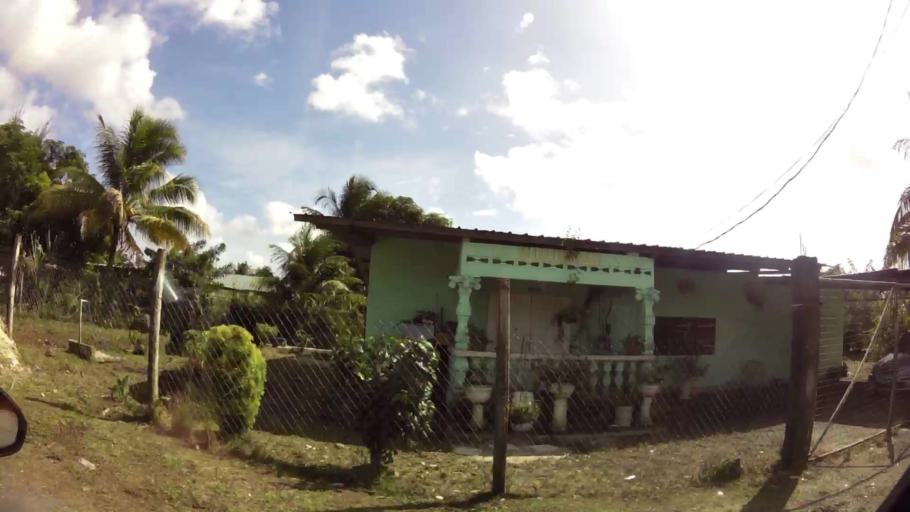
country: TT
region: Borough of Arima
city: Arima
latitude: 10.6232
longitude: -61.2575
